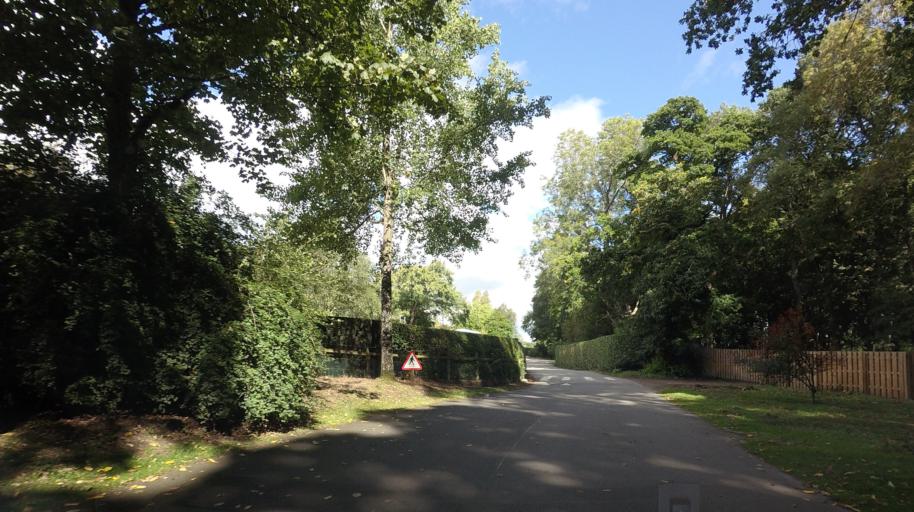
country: GB
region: Scotland
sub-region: Aberdeenshire
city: Banchory
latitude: 57.0602
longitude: -2.4385
